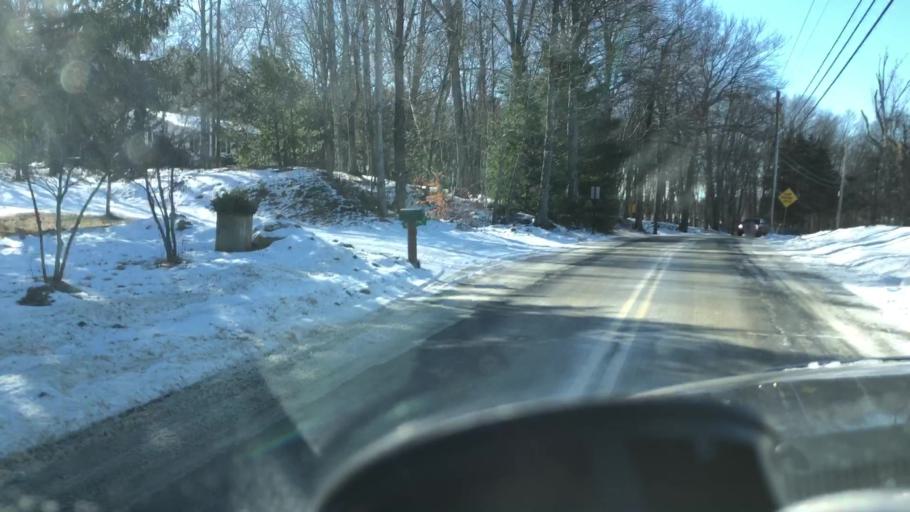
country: US
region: Massachusetts
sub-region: Hampshire County
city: Southampton
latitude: 42.2289
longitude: -72.7035
